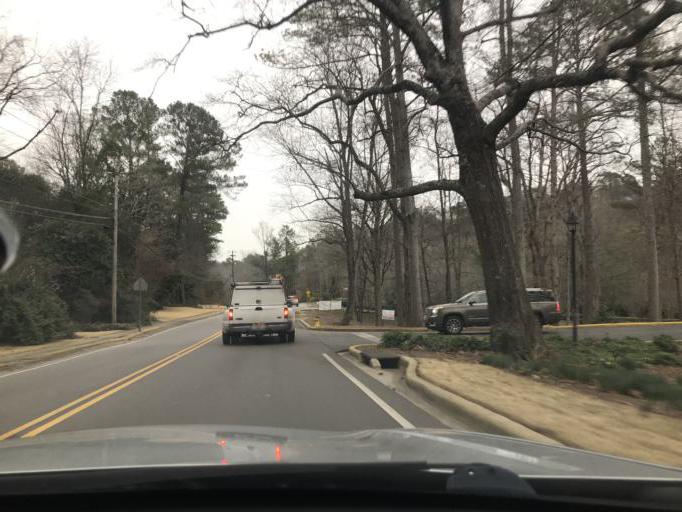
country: US
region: Alabama
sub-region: Jefferson County
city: Cahaba Heights
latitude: 33.4780
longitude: -86.7171
